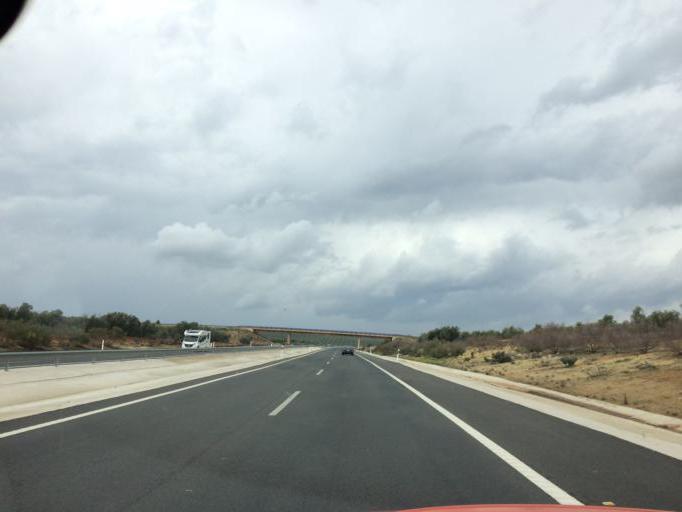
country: ES
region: Andalusia
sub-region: Provincia de Malaga
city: Antequera
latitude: 37.0864
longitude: -4.5405
